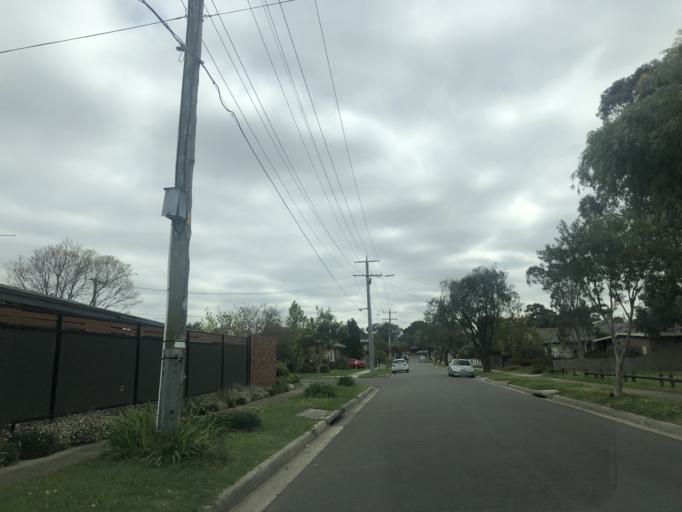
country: AU
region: Victoria
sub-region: Monash
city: Notting Hill
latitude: -37.9069
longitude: 145.1697
